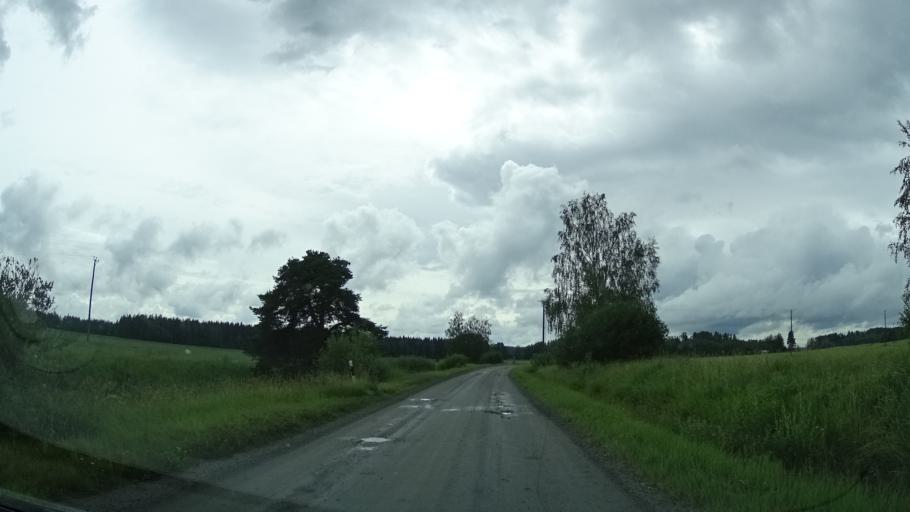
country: FI
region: Pirkanmaa
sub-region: Lounais-Pirkanmaa
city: Punkalaidun
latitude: 61.1184
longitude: 23.2915
